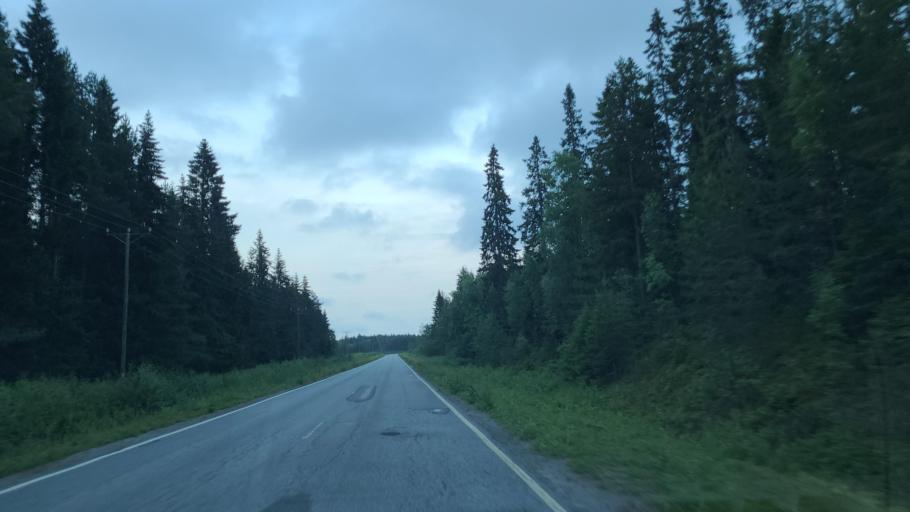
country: FI
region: Ostrobothnia
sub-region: Vaasa
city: Replot
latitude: 63.2247
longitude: 21.2349
